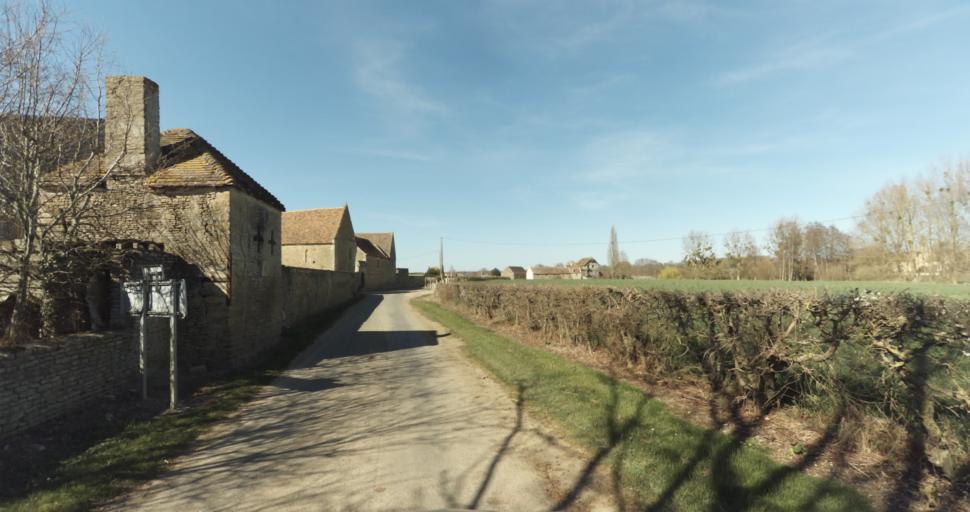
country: FR
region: Lower Normandy
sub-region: Departement du Calvados
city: Saint-Pierre-sur-Dives
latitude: 49.0497
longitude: -0.0268
